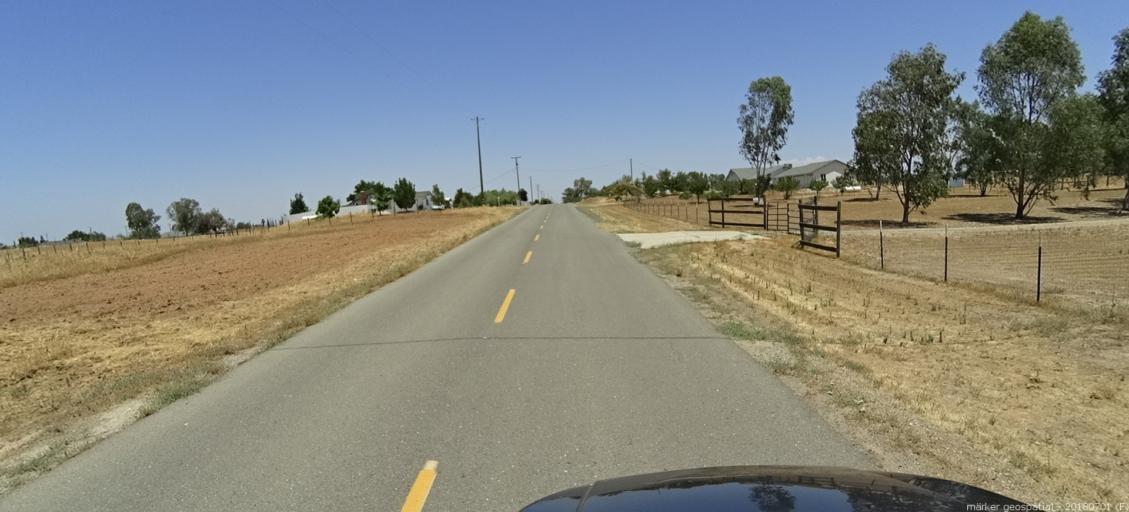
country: US
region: California
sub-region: Madera County
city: Madera Acres
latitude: 37.0359
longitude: -119.9957
